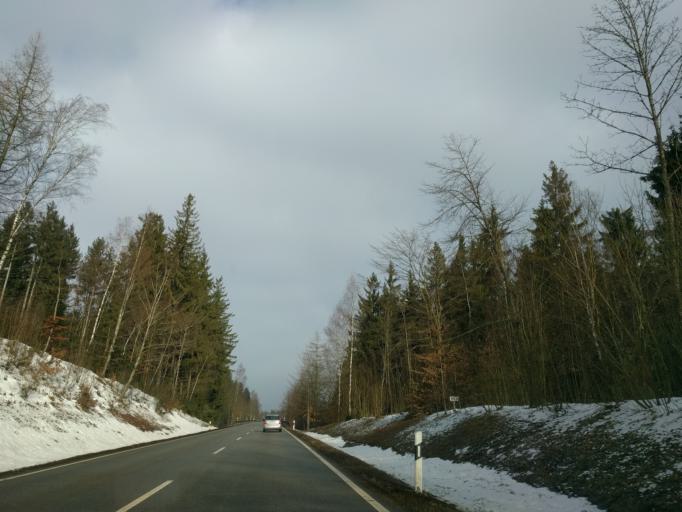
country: DE
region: Bavaria
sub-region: Lower Bavaria
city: Zwiesel
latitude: 49.0196
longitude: 13.2496
